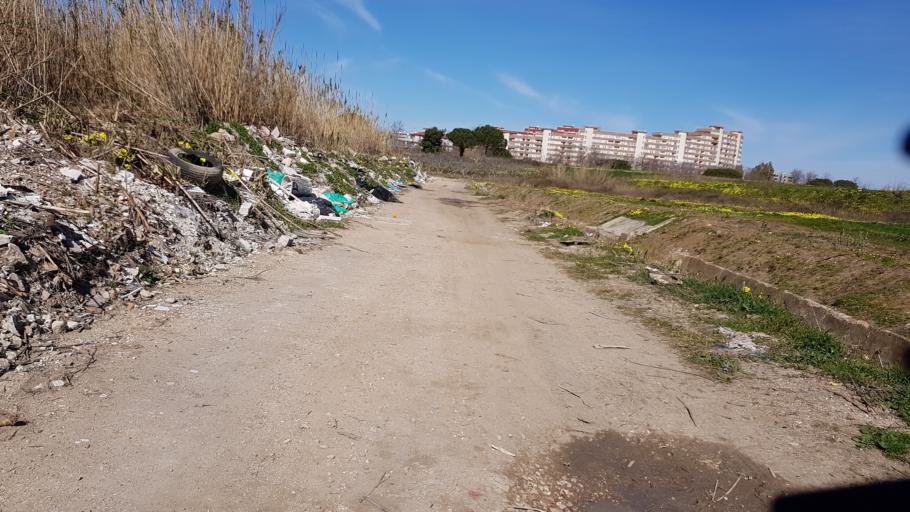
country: IT
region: Apulia
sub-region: Provincia di Brindisi
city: Brindisi
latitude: 40.6167
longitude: 17.9386
